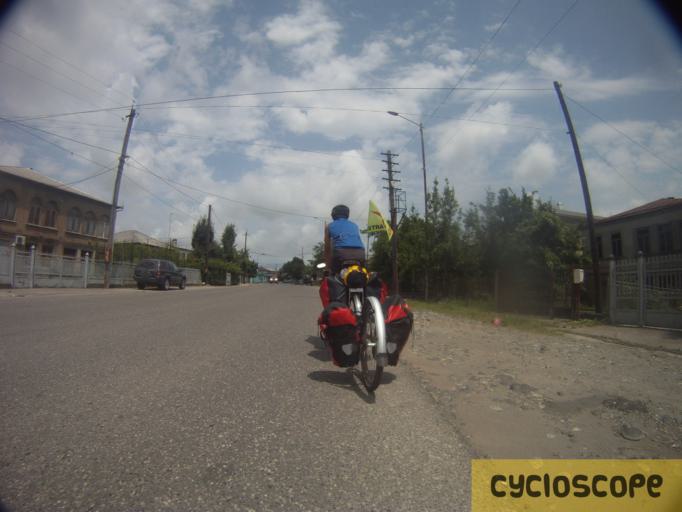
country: GE
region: Samegrelo and Zemo Svaneti
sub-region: Zugdidis Munitsip'alit'et'i
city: Zugdidi
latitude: 42.5063
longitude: 41.8697
